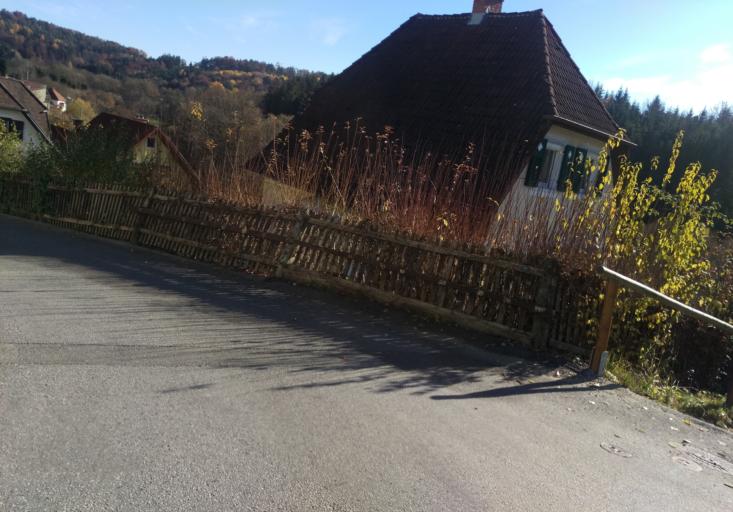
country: AT
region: Styria
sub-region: Graz Stadt
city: Mariatrost
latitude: 47.1097
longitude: 15.4923
